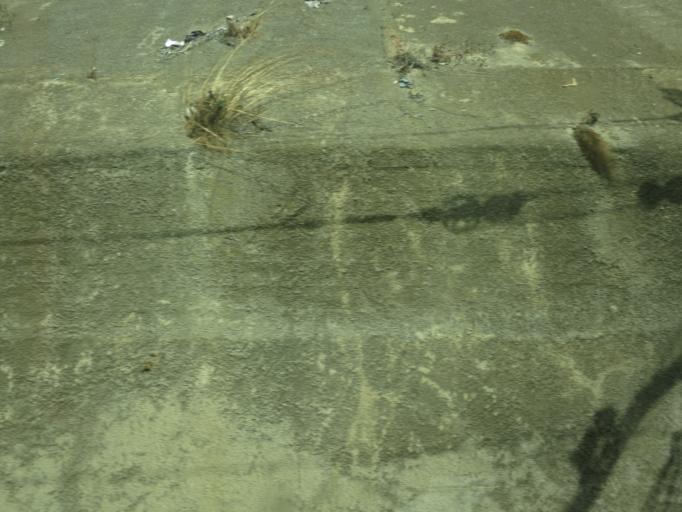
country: MA
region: Rabat-Sale-Zemmour-Zaer
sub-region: Rabat
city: Rabat
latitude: 34.0072
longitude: -6.8495
